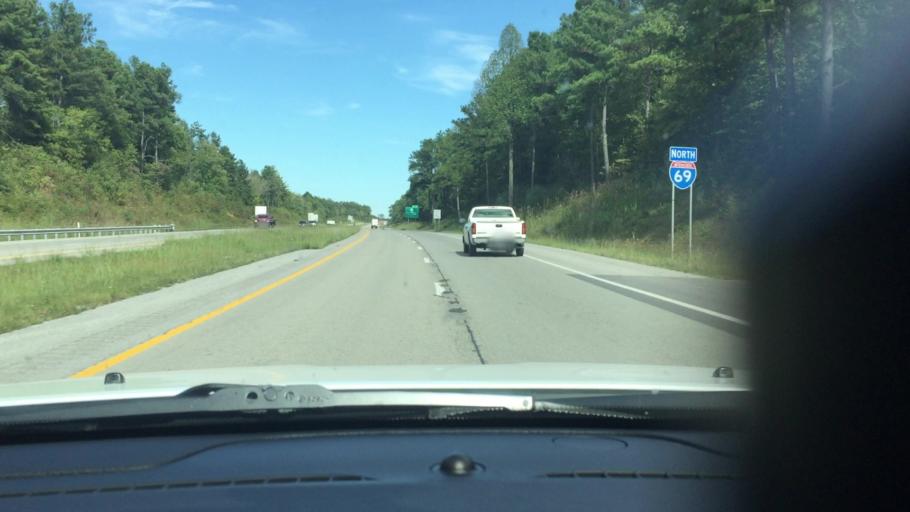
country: US
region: Kentucky
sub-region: Caldwell County
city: Princeton
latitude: 37.1249
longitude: -87.8867
